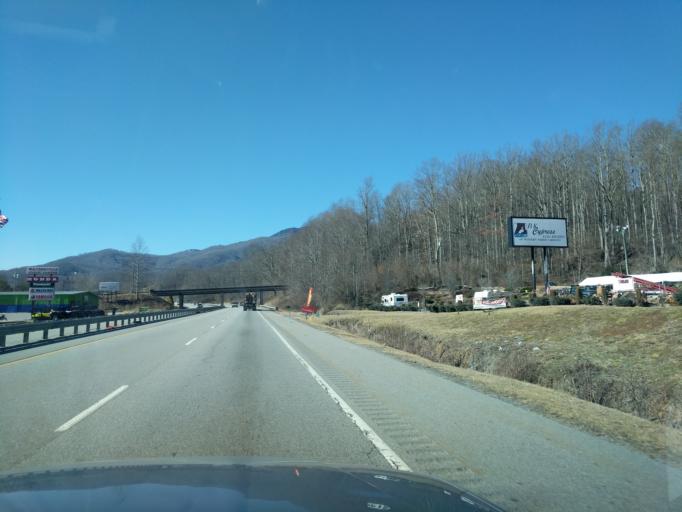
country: US
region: North Carolina
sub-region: Haywood County
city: Hazelwood
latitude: 35.4561
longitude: -83.0432
